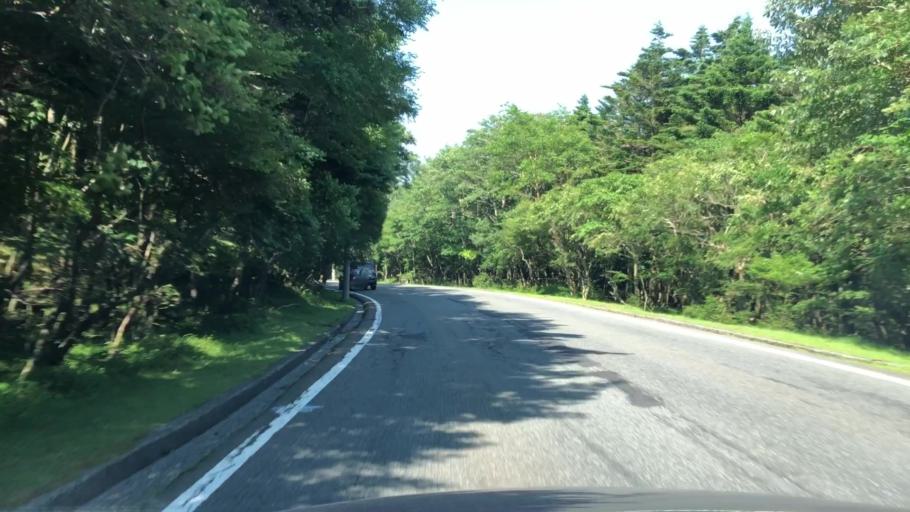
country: JP
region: Shizuoka
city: Gotemba
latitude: 35.3078
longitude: 138.7751
